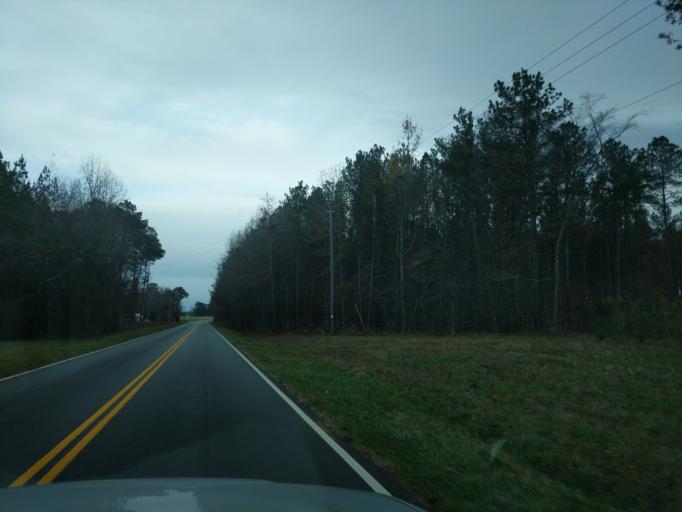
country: US
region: South Carolina
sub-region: Laurens County
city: Laurens
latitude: 34.3764
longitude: -82.0016
